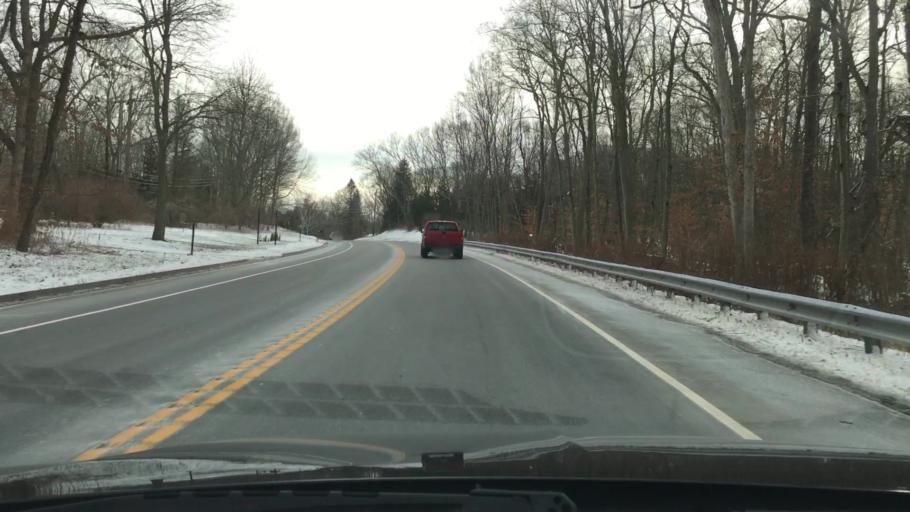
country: US
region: Connecticut
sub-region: New London County
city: Norwich
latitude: 41.4955
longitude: -72.0298
